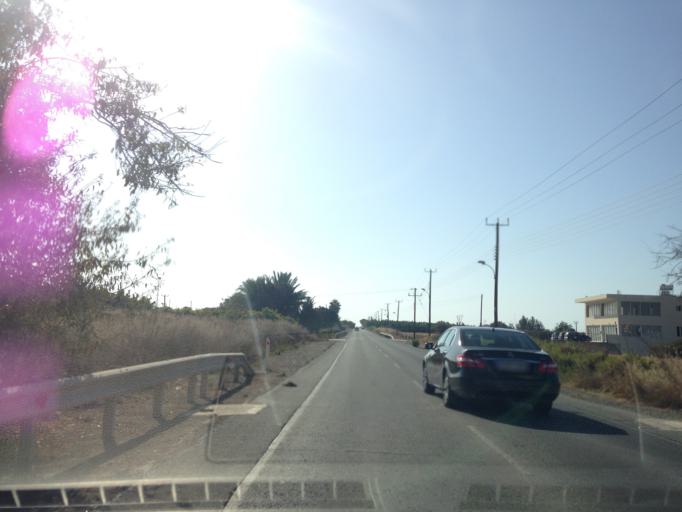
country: CY
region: Pafos
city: Pegeia
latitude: 34.8669
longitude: 32.3668
